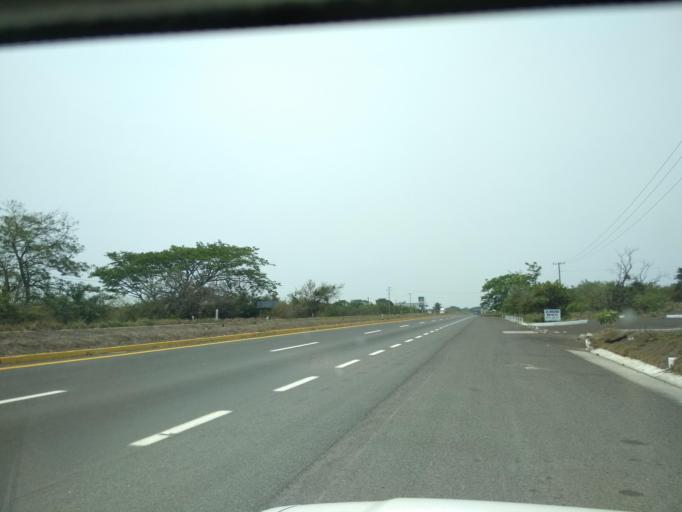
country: MX
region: Veracruz
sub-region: Veracruz
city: Delfino Victoria (Santa Fe)
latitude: 19.2223
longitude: -96.2582
